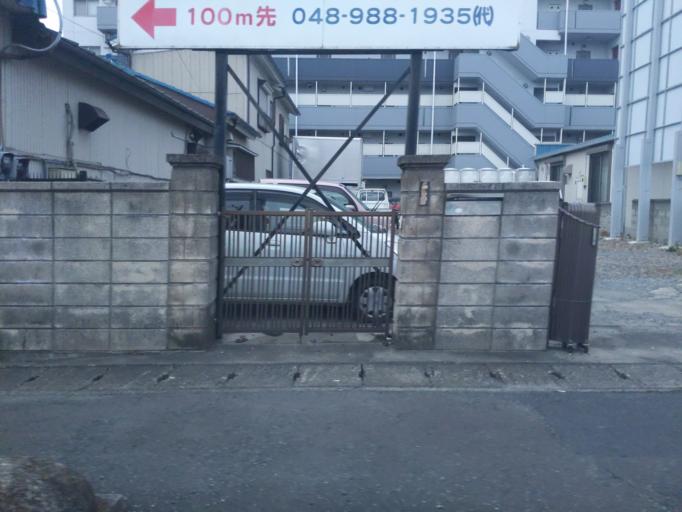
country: JP
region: Saitama
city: Koshigaya
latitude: 35.8650
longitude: 139.7950
